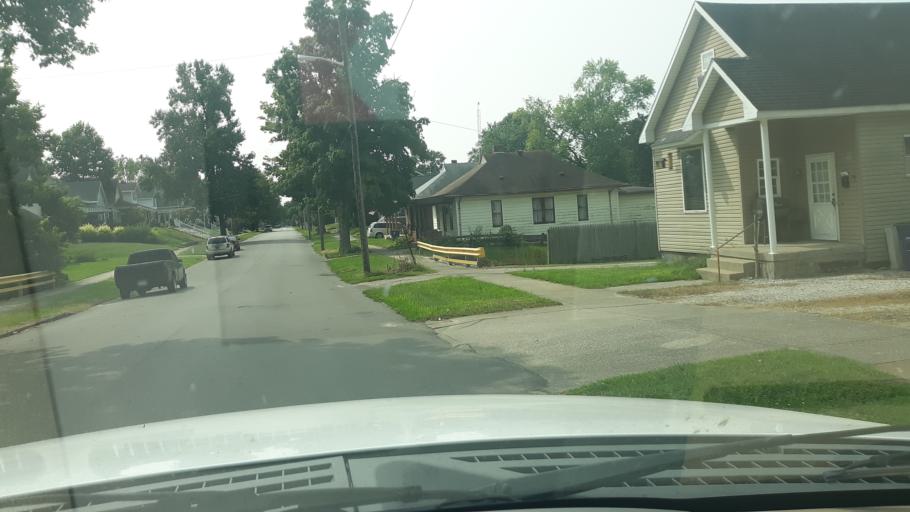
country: US
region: Indiana
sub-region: Gibson County
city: Princeton
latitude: 38.3532
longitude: -87.5638
